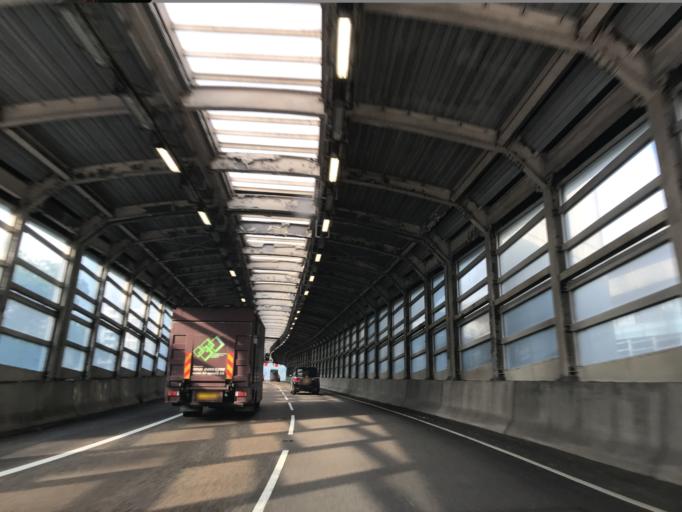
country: HK
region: Sham Shui Po
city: Sham Shui Po
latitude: 22.3328
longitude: 114.1443
